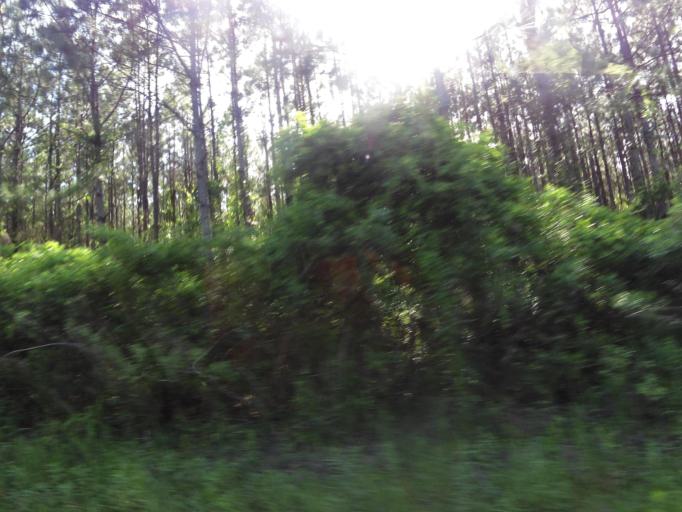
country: US
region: Florida
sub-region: Nassau County
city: Callahan
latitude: 30.5706
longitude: -81.7815
